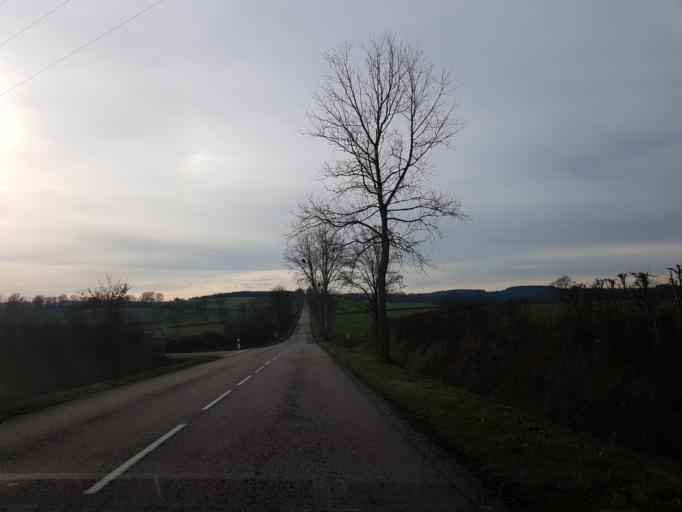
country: FR
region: Auvergne
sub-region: Departement de l'Allier
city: Souvigny
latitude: 46.4460
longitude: 3.1117
